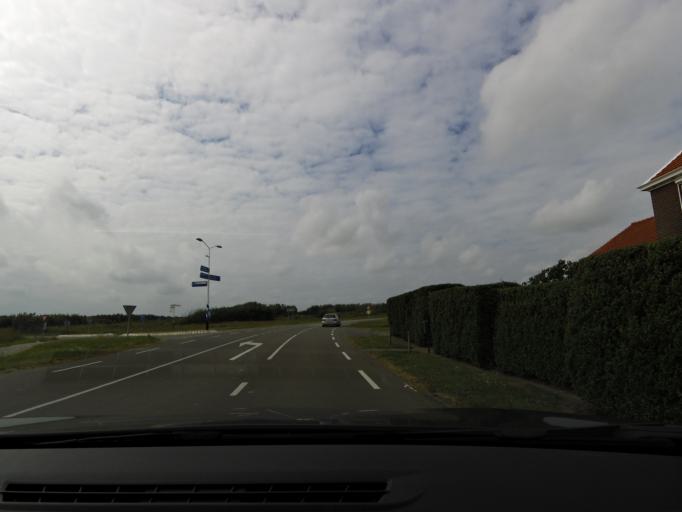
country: NL
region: Zeeland
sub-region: Gemeente Vlissingen
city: Vlissingen
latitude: 51.5124
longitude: 3.4660
